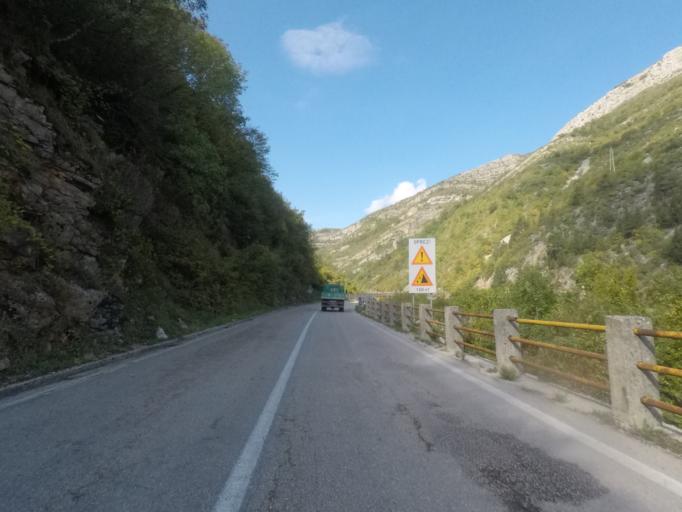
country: BA
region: Republika Srpska
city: Trebinje
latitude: 42.7074
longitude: 18.4539
